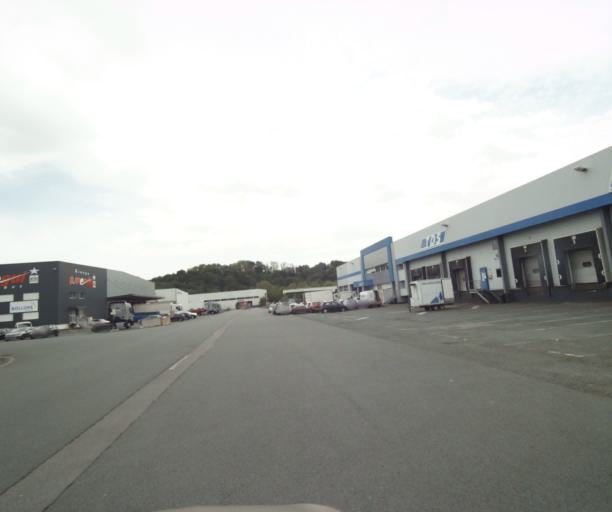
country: FR
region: Aquitaine
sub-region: Departement des Pyrenees-Atlantiques
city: Mouguerre
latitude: 43.4870
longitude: -1.4278
